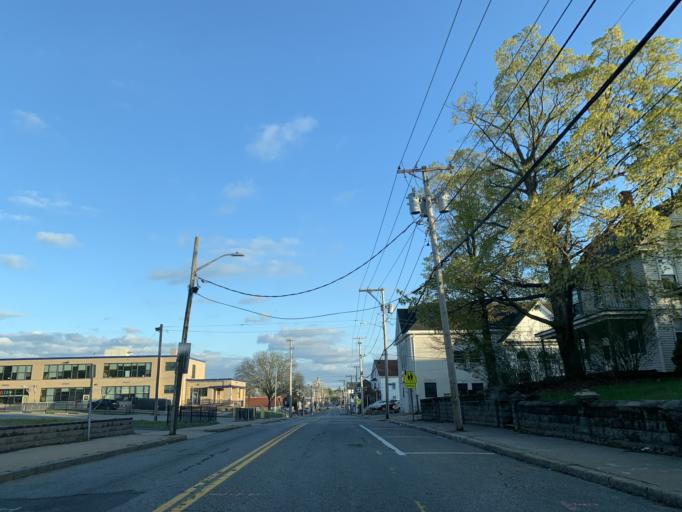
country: US
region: Rhode Island
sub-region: Providence County
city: Valley Falls
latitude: 41.9069
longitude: -71.3931
